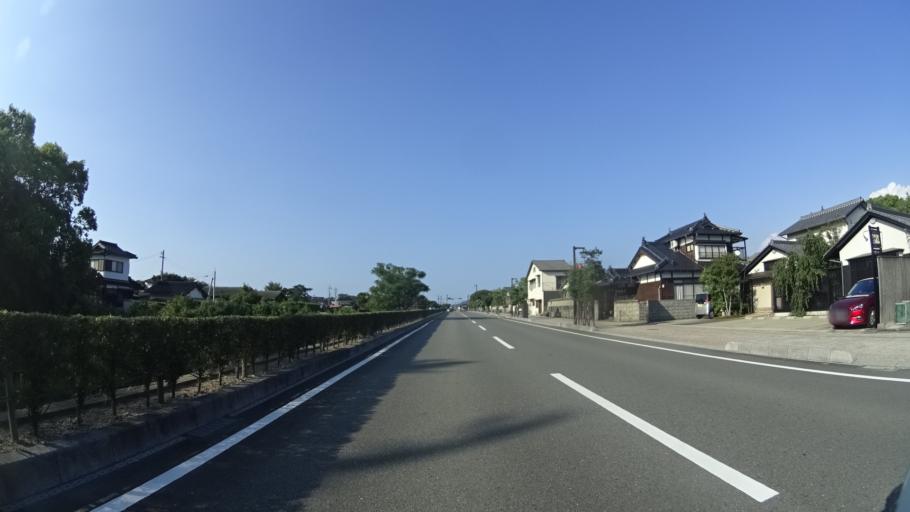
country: JP
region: Yamaguchi
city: Hagi
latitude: 34.4113
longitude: 131.3918
